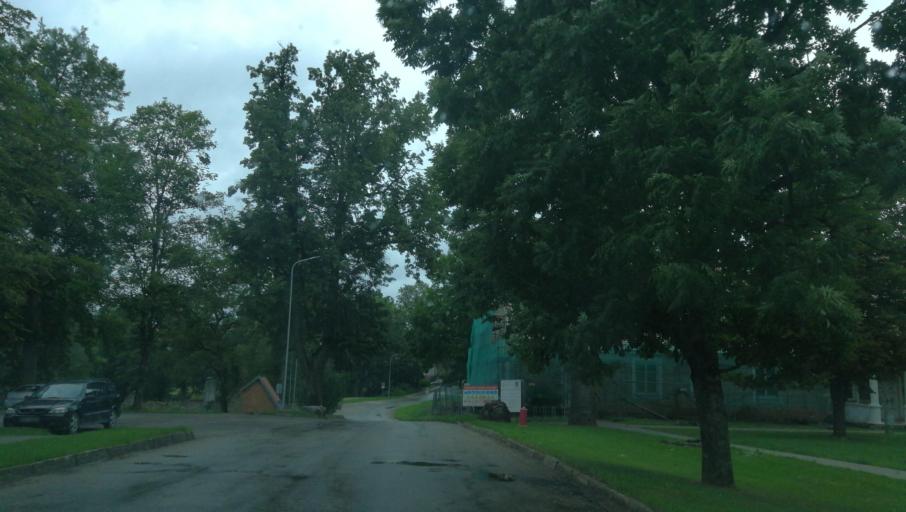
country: LV
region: Beverina
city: Murmuiza
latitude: 57.4746
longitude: 25.4900
